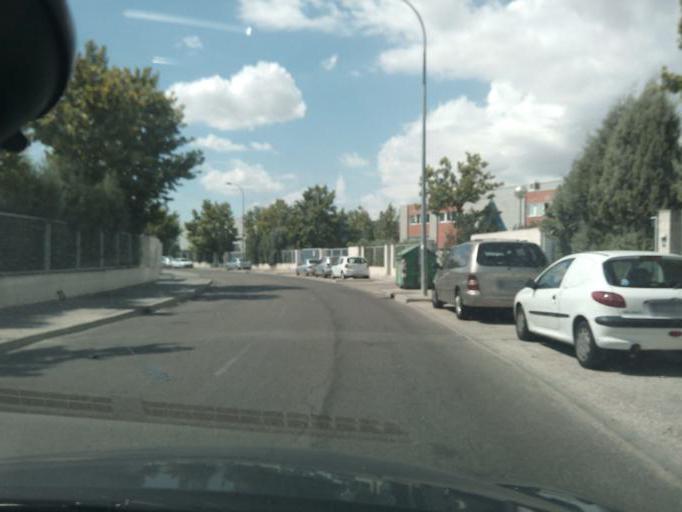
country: ES
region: Madrid
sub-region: Provincia de Madrid
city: Torrejon de Ardoz
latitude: 40.4503
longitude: -3.4877
